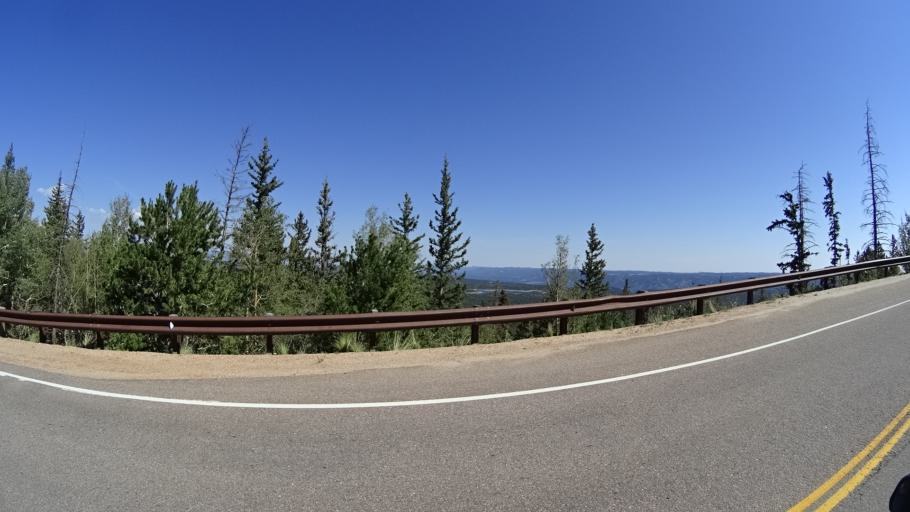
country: US
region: Colorado
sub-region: El Paso County
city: Cascade-Chipita Park
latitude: 38.8954
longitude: -105.0622
